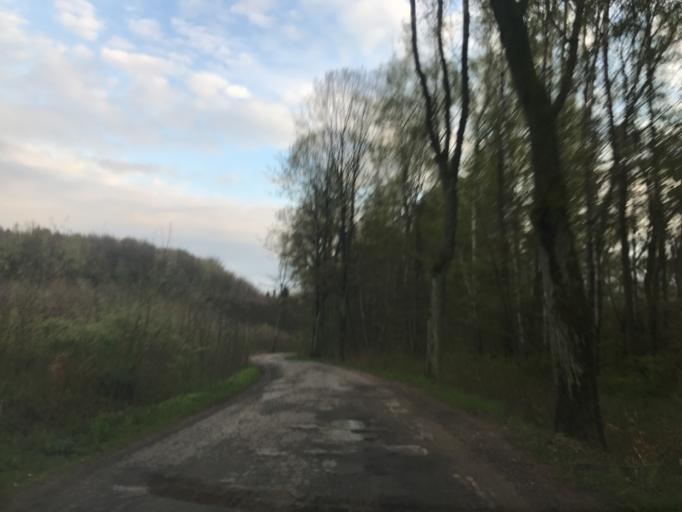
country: PL
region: Warmian-Masurian Voivodeship
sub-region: Powiat ilawski
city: Lubawa
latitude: 53.5534
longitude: 19.8968
